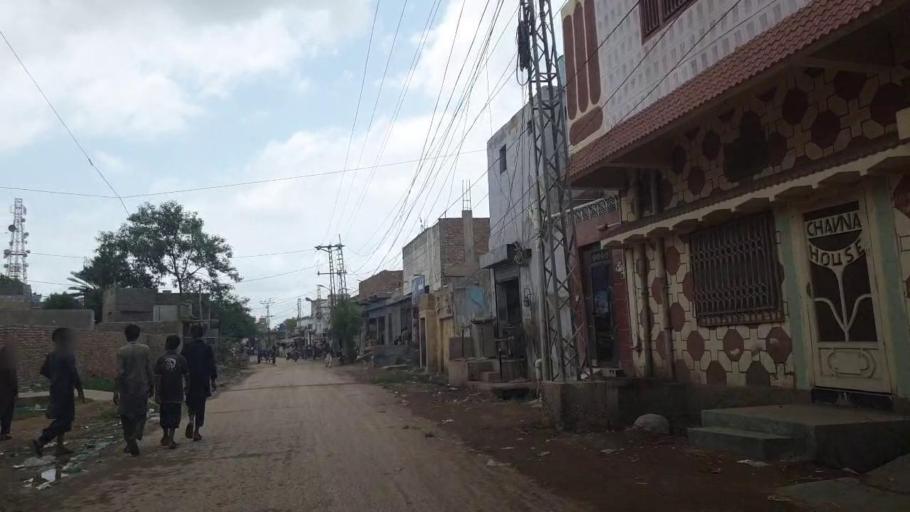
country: PK
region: Sindh
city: Badin
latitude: 24.6560
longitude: 68.8446
